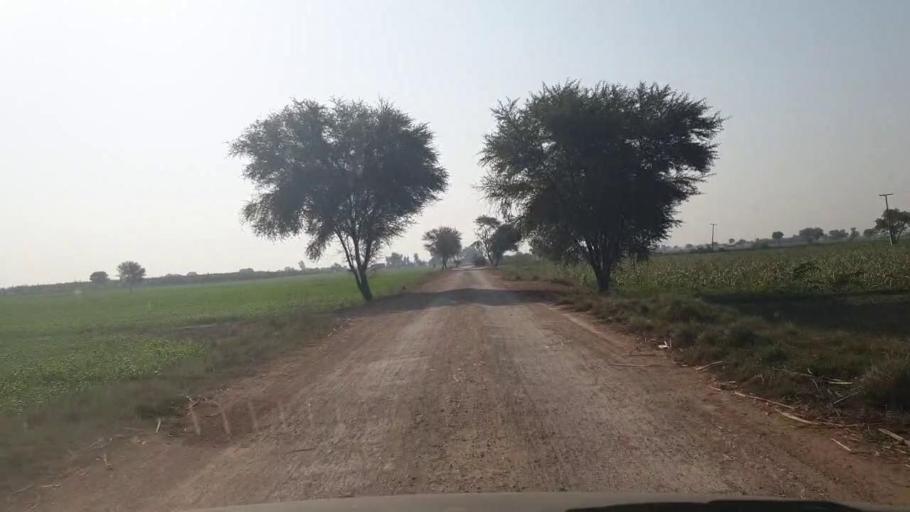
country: PK
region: Sindh
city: Bhit Shah
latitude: 25.7525
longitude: 68.5618
